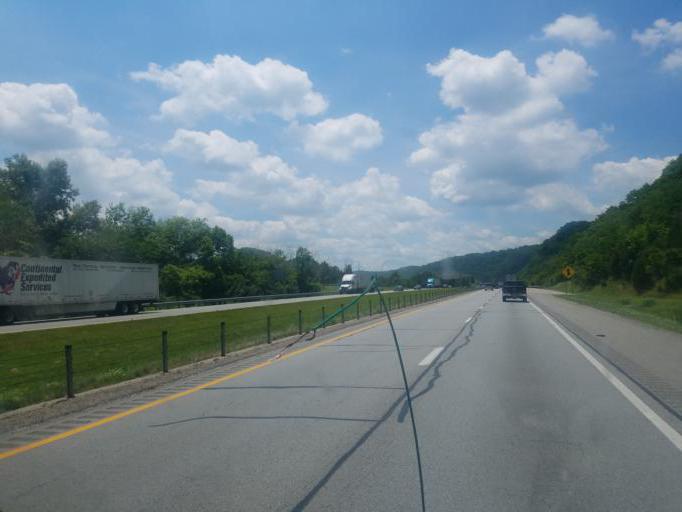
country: US
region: Kentucky
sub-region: Carroll County
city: Carrollton
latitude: 38.6308
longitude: -85.1412
